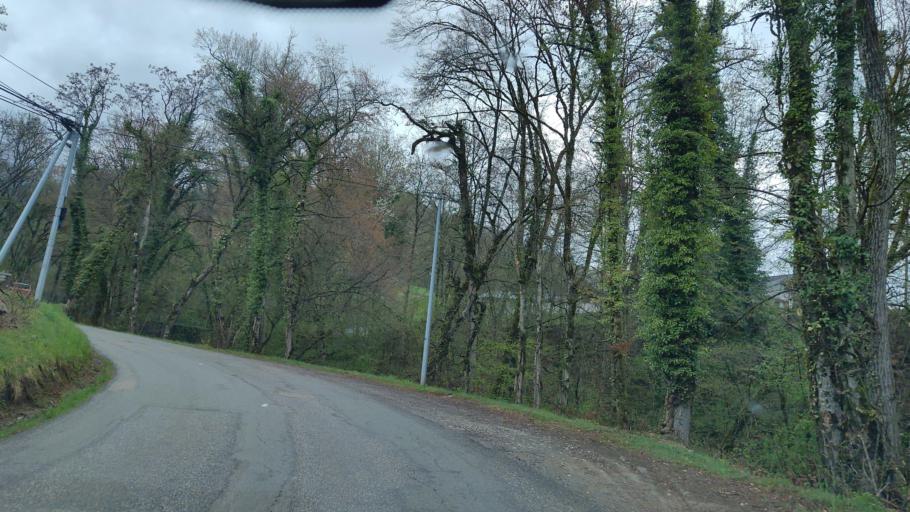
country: FR
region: Rhone-Alpes
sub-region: Departement de la Savoie
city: Frontenex
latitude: 45.6418
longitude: 6.3068
